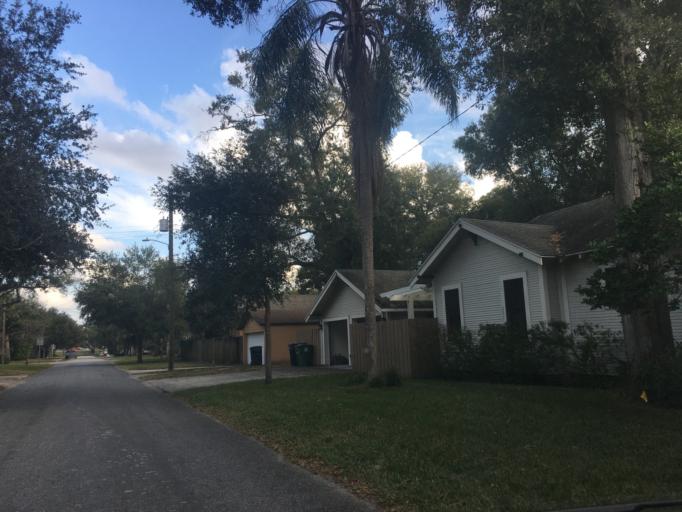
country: US
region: Florida
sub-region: Hillsborough County
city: Tampa
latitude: 27.9988
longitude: -82.4563
